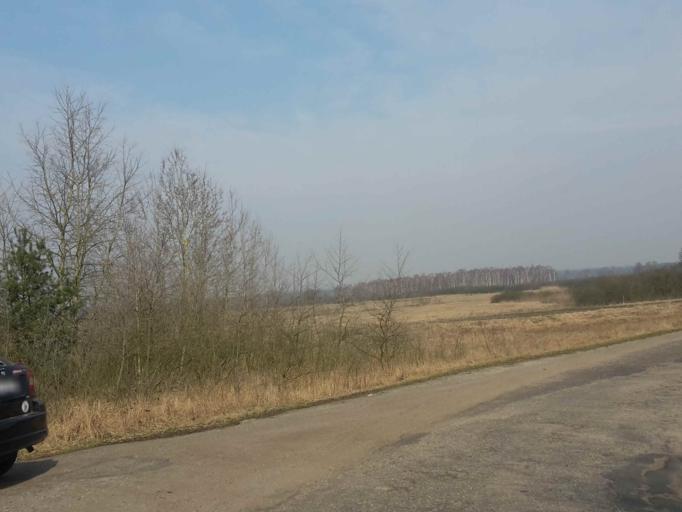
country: PL
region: Kujawsko-Pomorskie
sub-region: Powiat nakielski
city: Sadki
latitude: 53.0937
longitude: 17.4195
